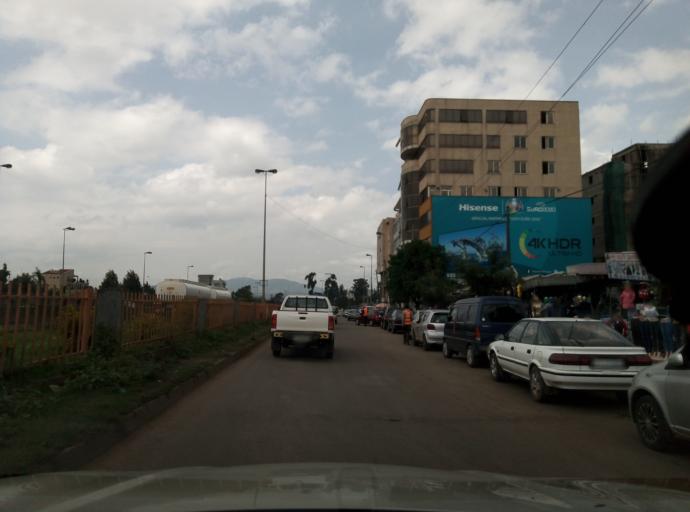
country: ET
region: Adis Abeba
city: Addis Ababa
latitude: 9.0082
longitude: 38.7195
